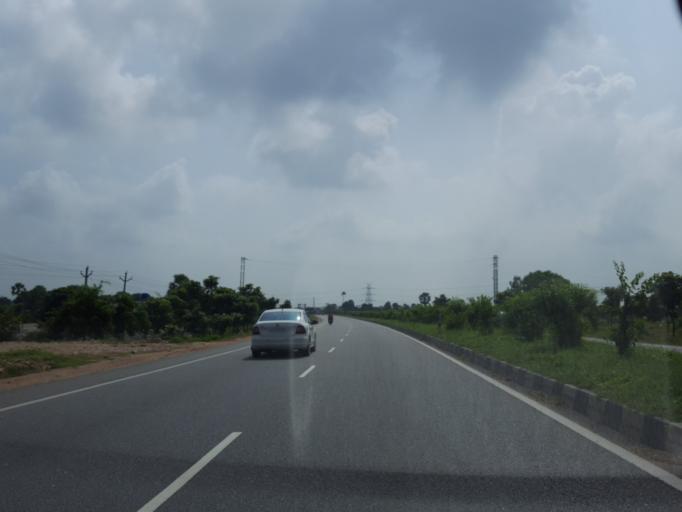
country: IN
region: Telangana
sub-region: Nalgonda
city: Gudur
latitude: 17.2658
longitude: 78.8304
